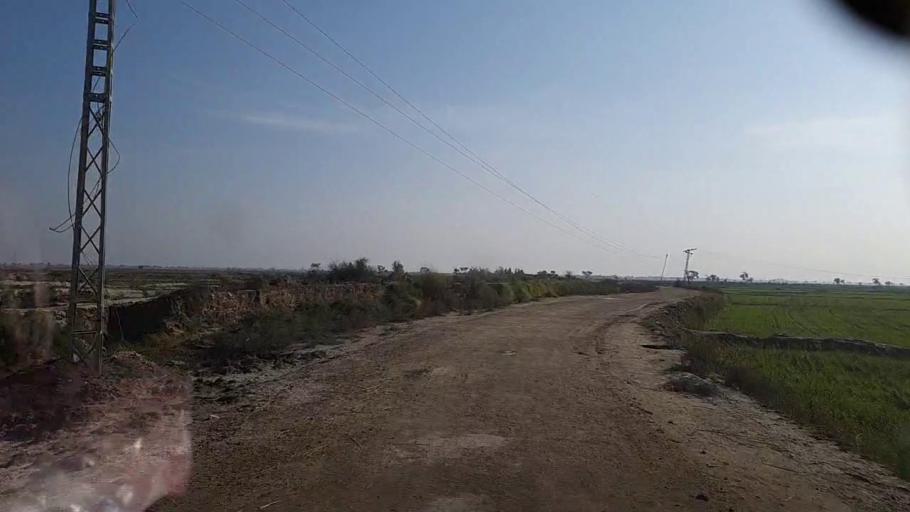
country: PK
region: Sindh
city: Jacobabad
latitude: 28.2969
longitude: 68.5579
